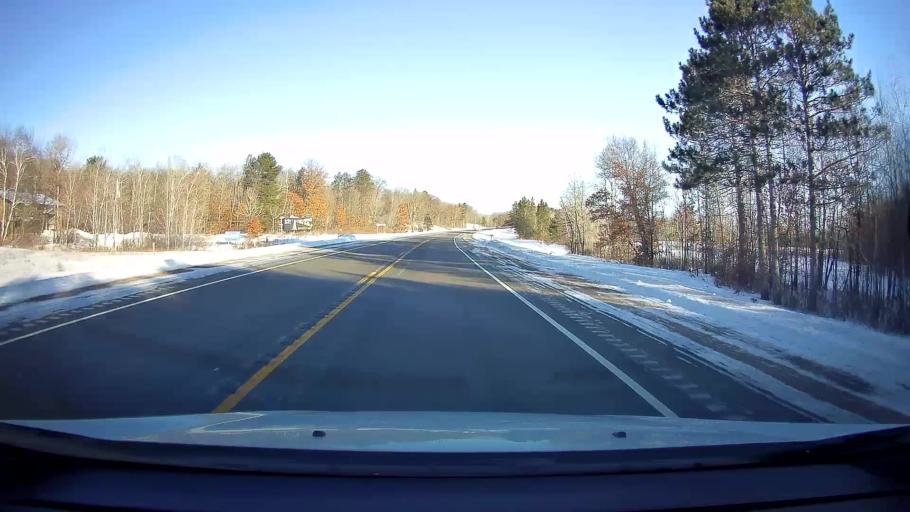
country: US
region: Wisconsin
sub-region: Sawyer County
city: Hayward
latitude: 46.0577
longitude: -91.4405
